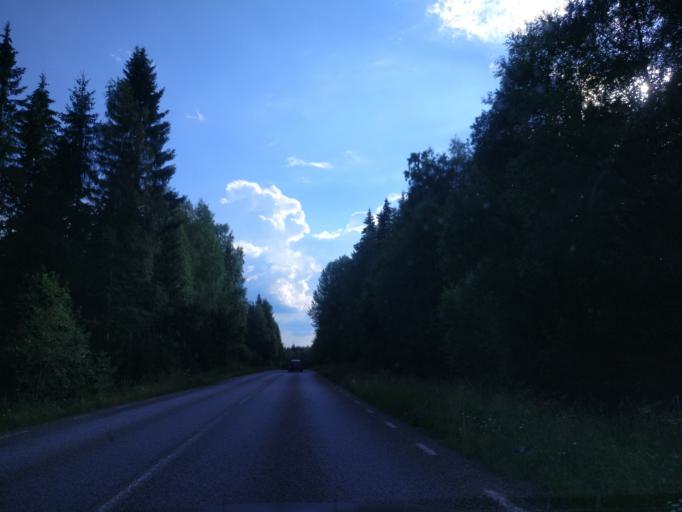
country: SE
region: Dalarna
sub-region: Ludvika Kommun
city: Ludvika
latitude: 60.2782
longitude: 15.0817
